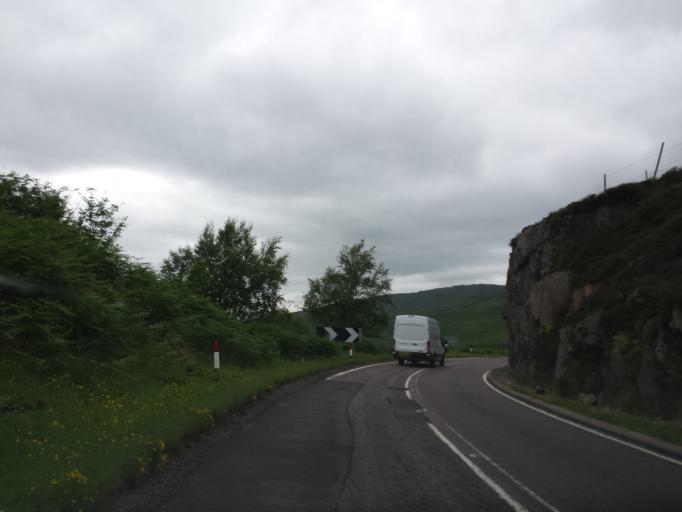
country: GB
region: Scotland
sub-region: Highland
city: Fort William
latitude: 56.8783
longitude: -5.5772
